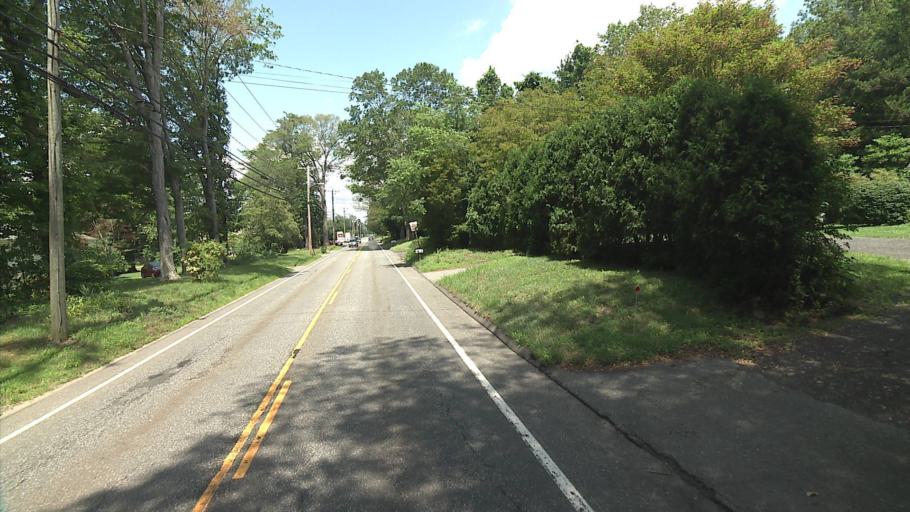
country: US
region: Connecticut
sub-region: Middlesex County
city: Chester Center
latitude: 41.4177
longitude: -72.4431
